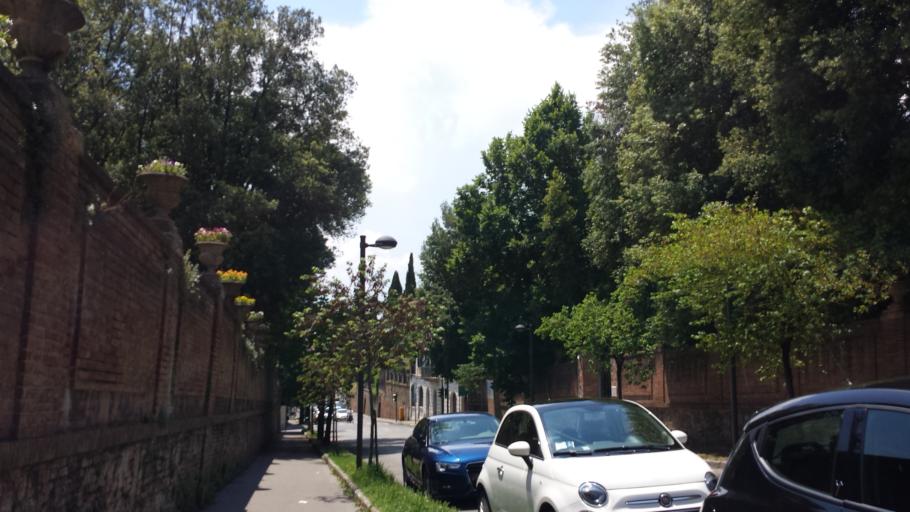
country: IT
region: Tuscany
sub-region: Provincia di Siena
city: Siena
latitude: 43.3125
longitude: 11.3394
